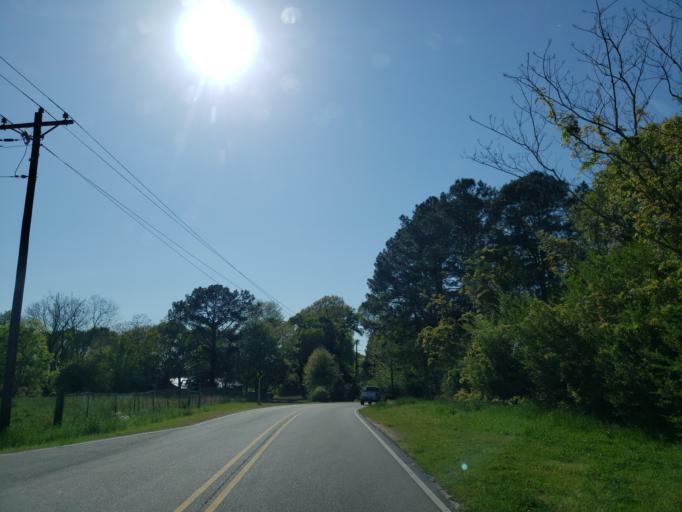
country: US
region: Mississippi
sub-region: Covington County
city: Collins
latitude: 31.6127
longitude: -89.3864
